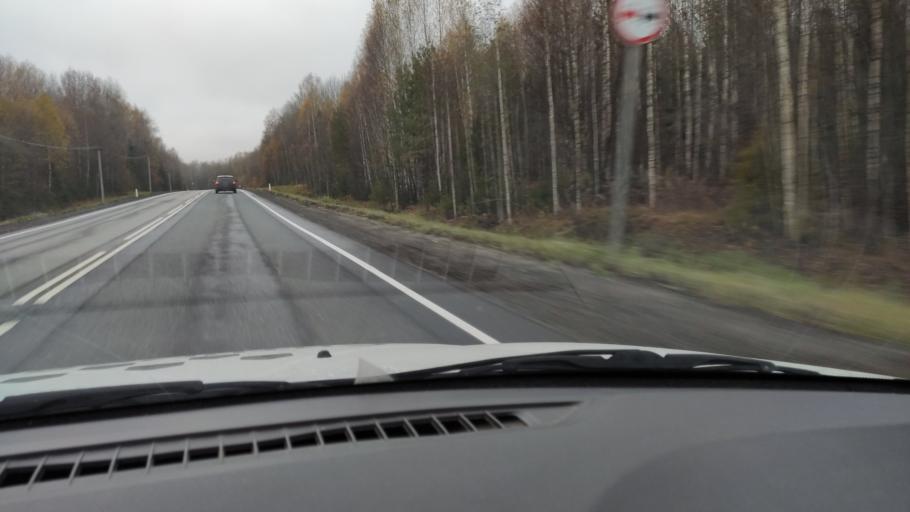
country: RU
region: Kirov
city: Belaya Kholunitsa
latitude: 58.9205
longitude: 51.1210
